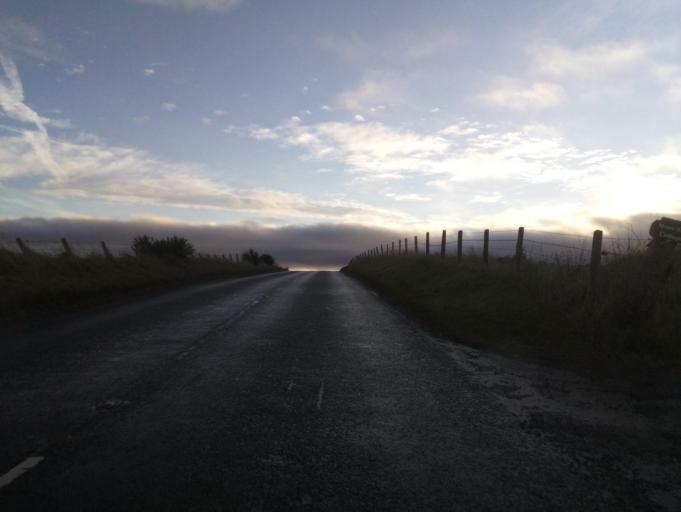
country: GB
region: Scotland
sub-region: Angus
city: Letham
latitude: 56.5760
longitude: -2.7800
